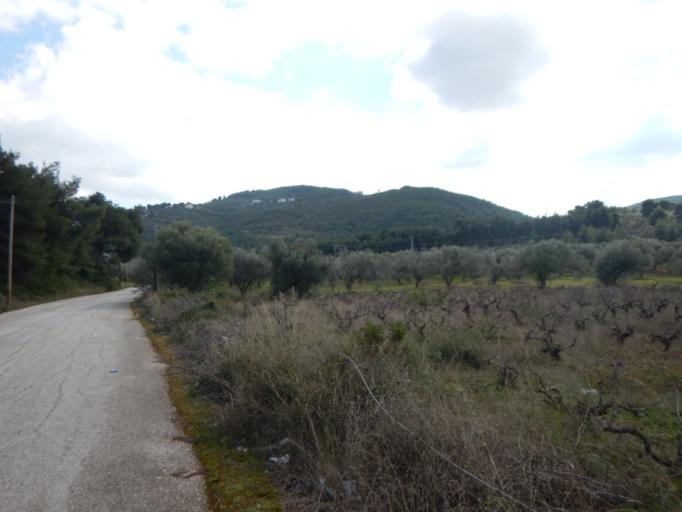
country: GR
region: Attica
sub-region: Nomarchia Anatolikis Attikis
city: Markopoulo Oropou
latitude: 38.2951
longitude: 23.8432
